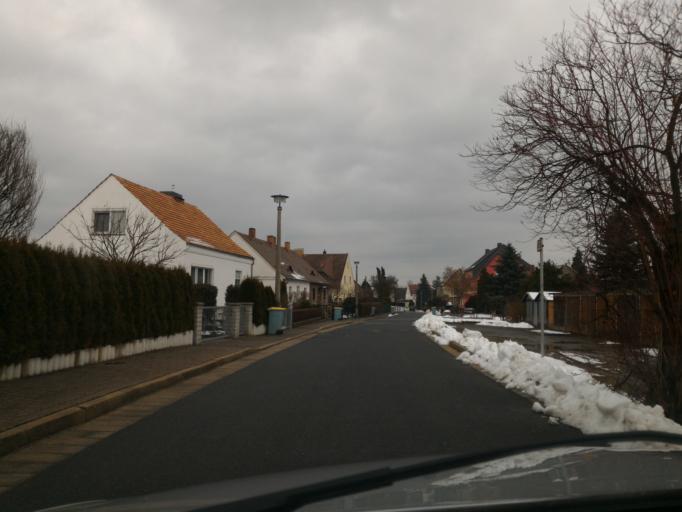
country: DE
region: Saxony
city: Mittelherwigsdorf
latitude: 50.9024
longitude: 14.7635
